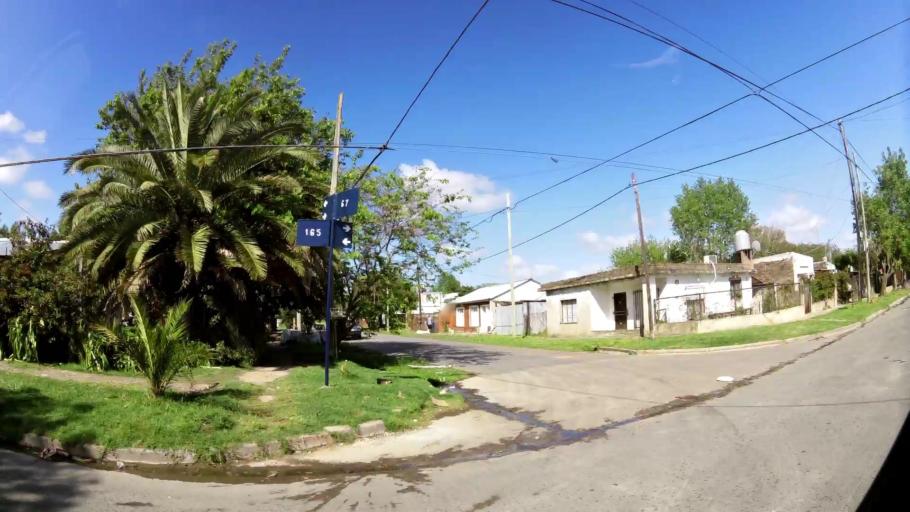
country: AR
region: Buenos Aires
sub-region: Partido de Quilmes
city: Quilmes
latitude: -34.7927
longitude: -58.1430
